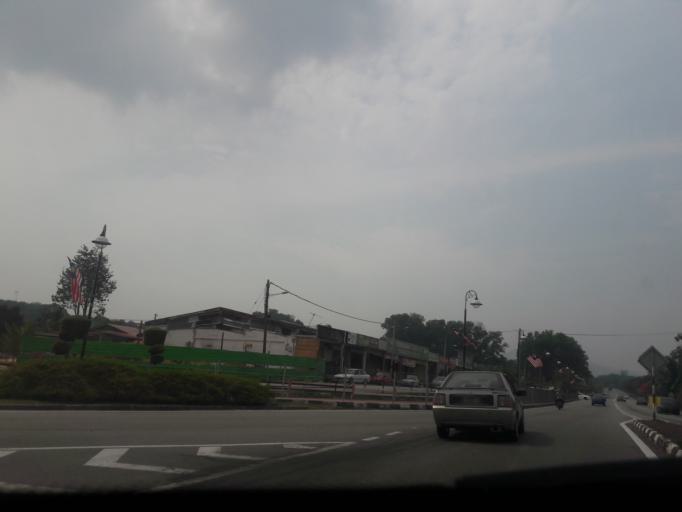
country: MY
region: Kedah
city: Kulim
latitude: 5.3762
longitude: 100.5396
